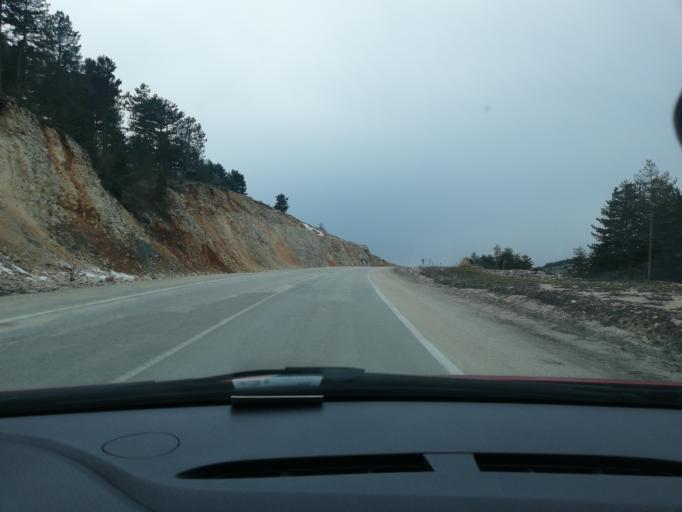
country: TR
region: Kastamonu
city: Pinarbasi
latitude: 41.5596
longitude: 33.0846
